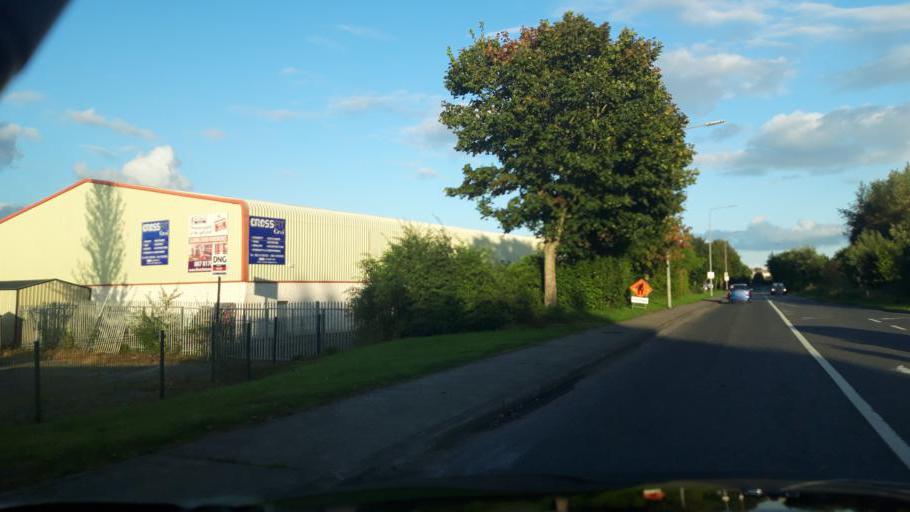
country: IE
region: Leinster
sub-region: An Iarmhi
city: Athlone
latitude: 53.4273
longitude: -7.9015
